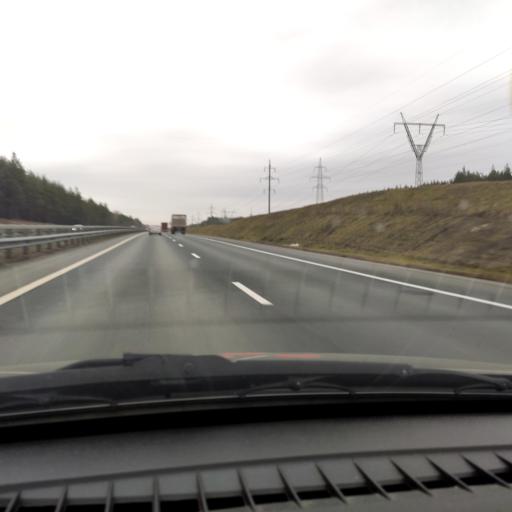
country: RU
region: Samara
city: Povolzhskiy
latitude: 53.5166
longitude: 49.7298
